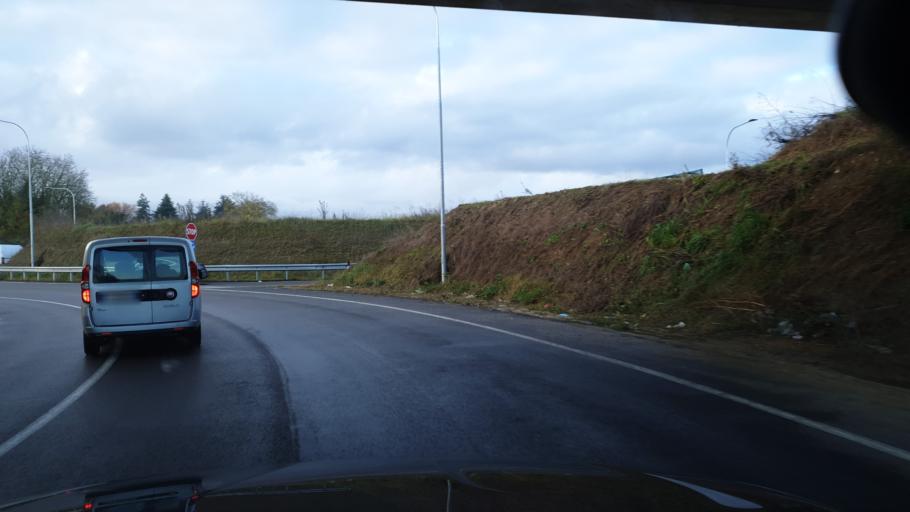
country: IT
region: Emilia-Romagna
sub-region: Provincia di Bologna
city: Crespellano
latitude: 44.5200
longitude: 11.1391
